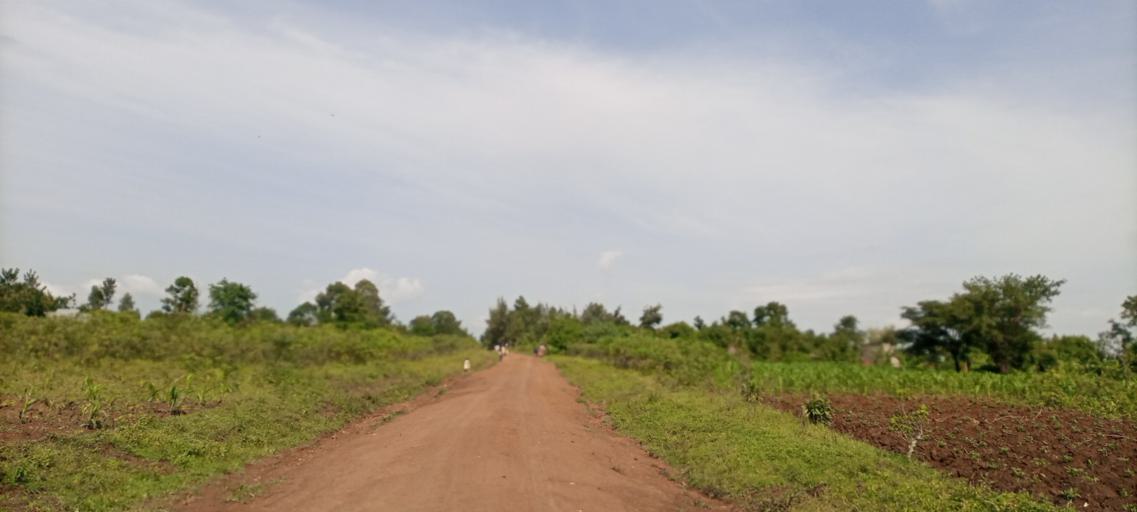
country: UG
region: Eastern Region
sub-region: Mbale District
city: Mbale
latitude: 1.1354
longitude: 34.0567
